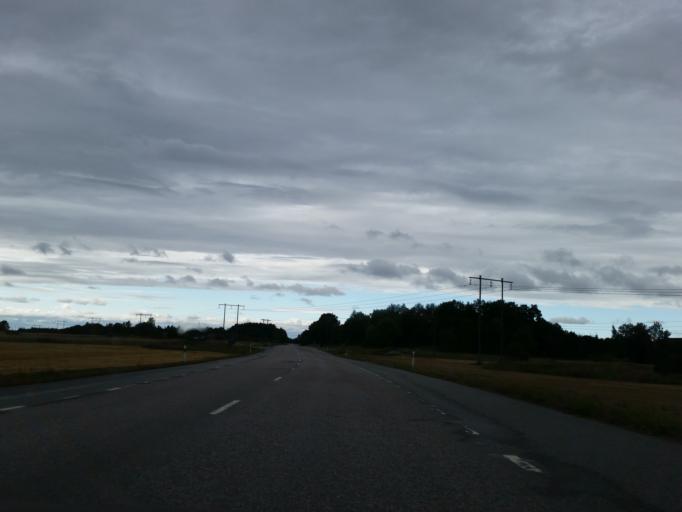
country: SE
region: Uppsala
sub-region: Enkopings Kommun
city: Orsundsbro
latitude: 59.6579
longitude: 17.3413
